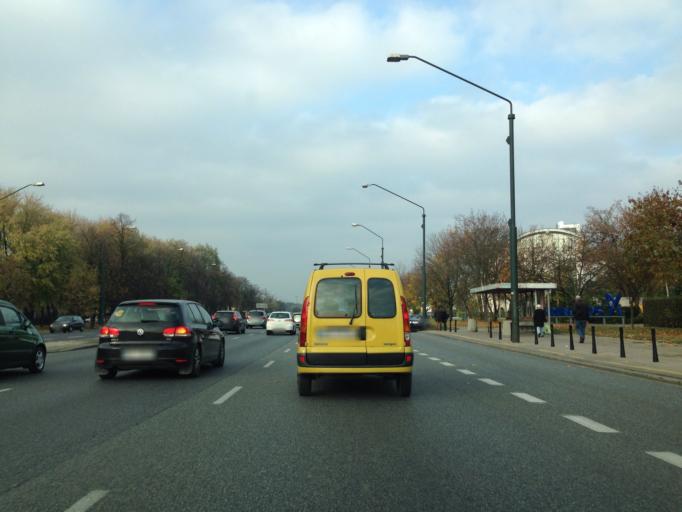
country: PL
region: Masovian Voivodeship
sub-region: Warszawa
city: Ursynow
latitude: 52.1476
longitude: 21.0178
